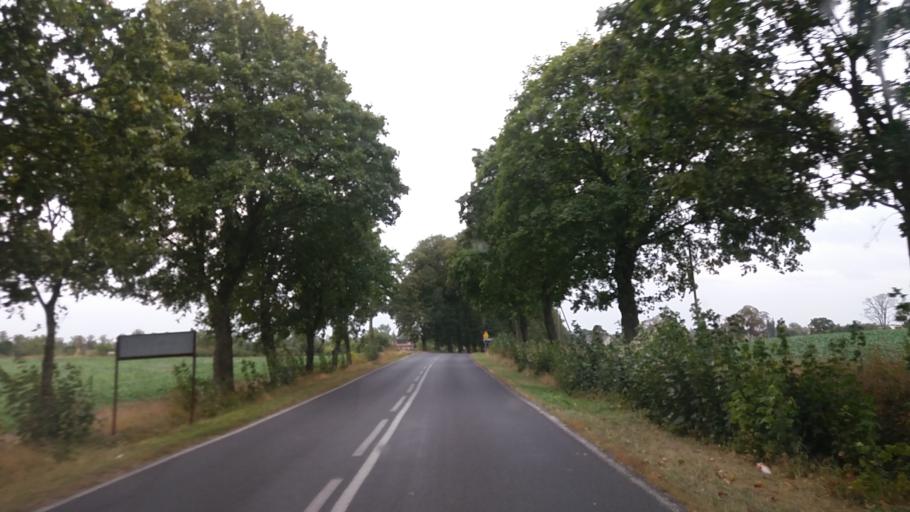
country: PL
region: Lubusz
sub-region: Powiat strzelecko-drezdenecki
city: Strzelce Krajenskie
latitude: 52.8871
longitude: 15.5412
